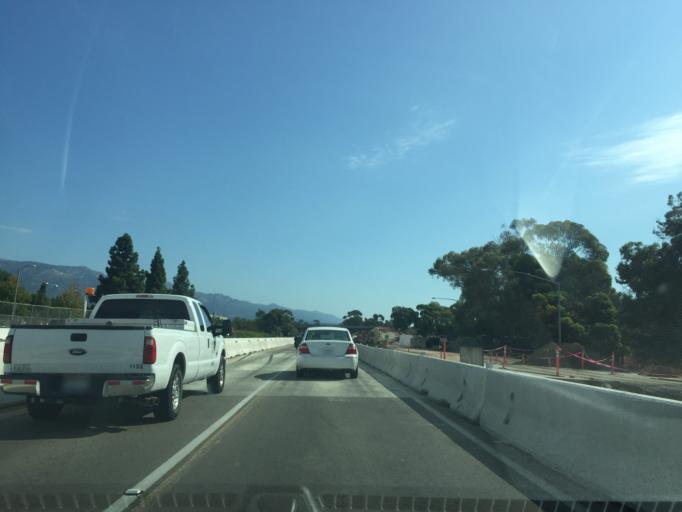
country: US
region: California
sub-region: Santa Barbara County
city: Goleta
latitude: 34.4391
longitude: -119.8375
